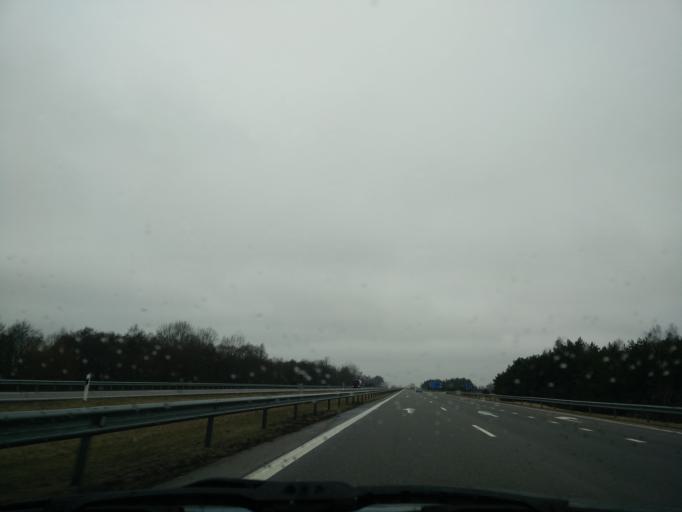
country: LT
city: Kelme
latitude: 55.3955
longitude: 22.8716
